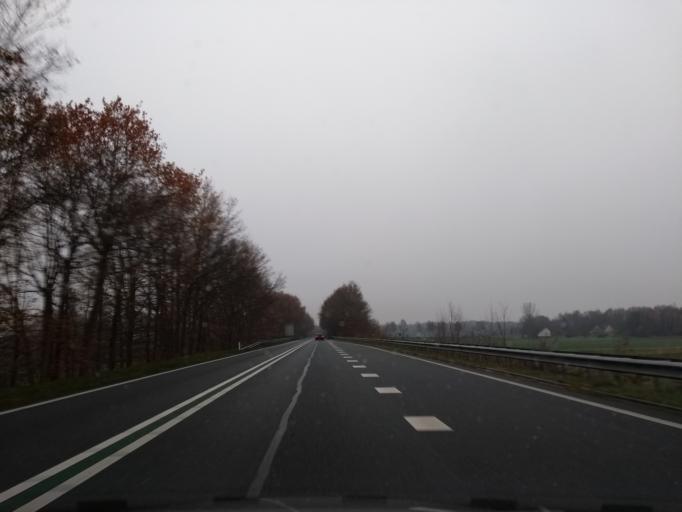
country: NL
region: Overijssel
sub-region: Gemeente Twenterand
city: Vroomshoop
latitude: 52.5005
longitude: 6.5766
